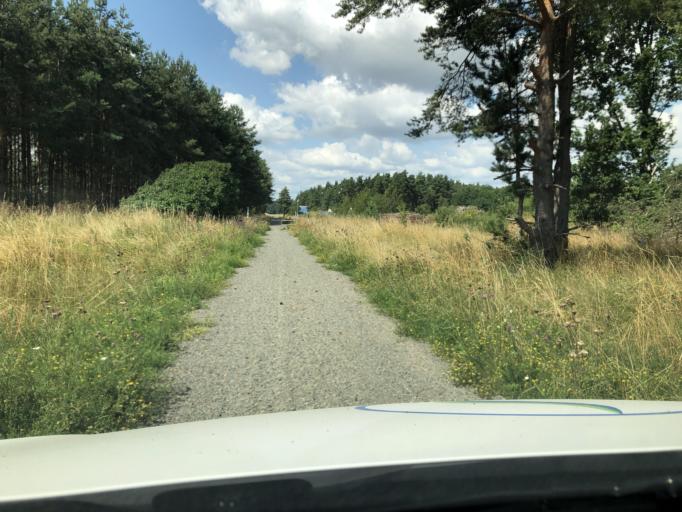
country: SE
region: Skane
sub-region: Kristianstads Kommun
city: Degeberga
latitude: 55.8510
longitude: 14.0918
